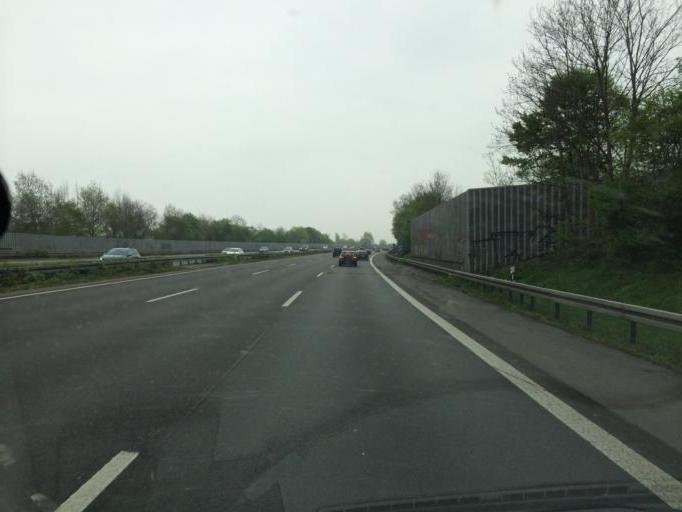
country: DE
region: North Rhine-Westphalia
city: Castrop-Rauxel
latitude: 51.6039
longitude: 7.3105
